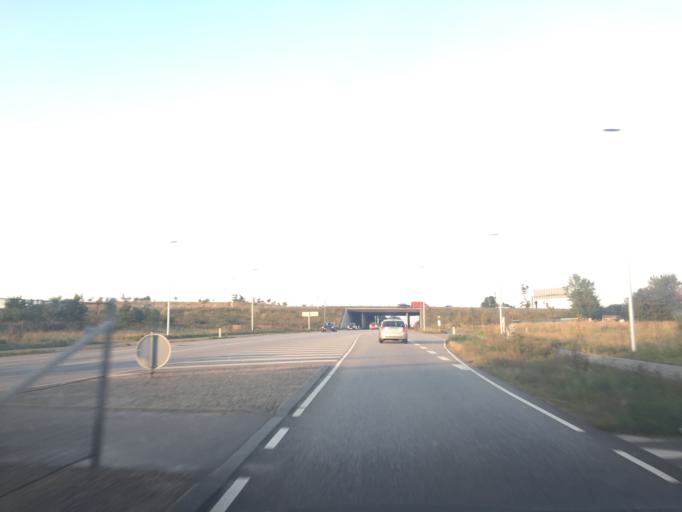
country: DK
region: Zealand
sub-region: Roskilde Kommune
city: Roskilde
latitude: 55.6237
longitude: 12.0586
